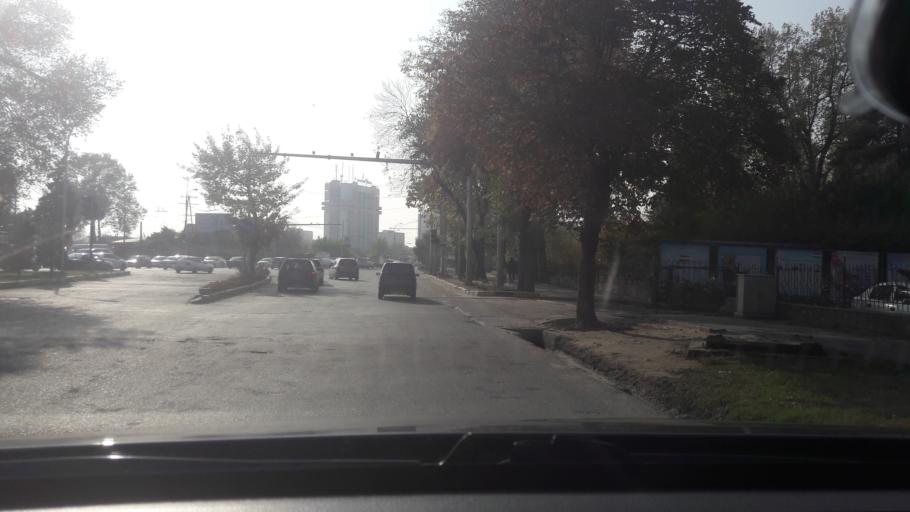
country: TJ
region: Dushanbe
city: Dushanbe
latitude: 38.5615
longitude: 68.7746
